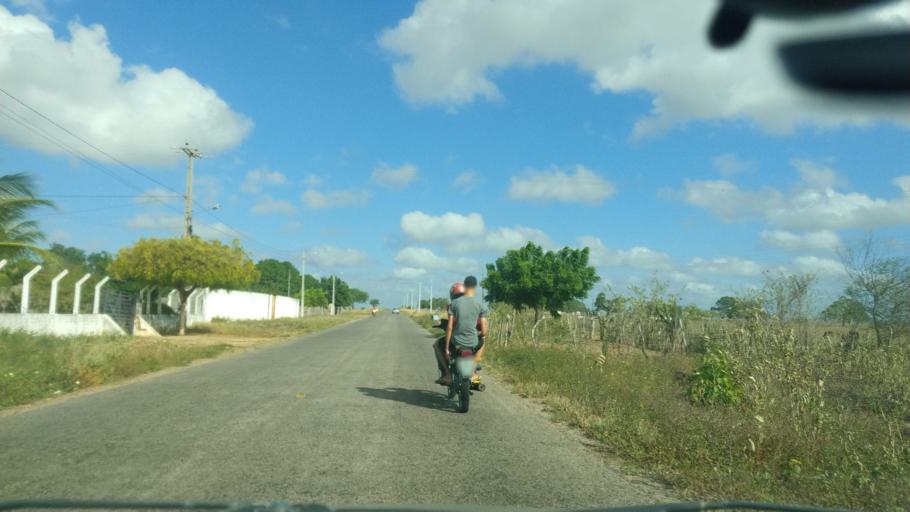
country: BR
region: Rio Grande do Norte
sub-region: Sao Paulo Do Potengi
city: Sao Paulo do Potengi
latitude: -5.9149
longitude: -35.7380
